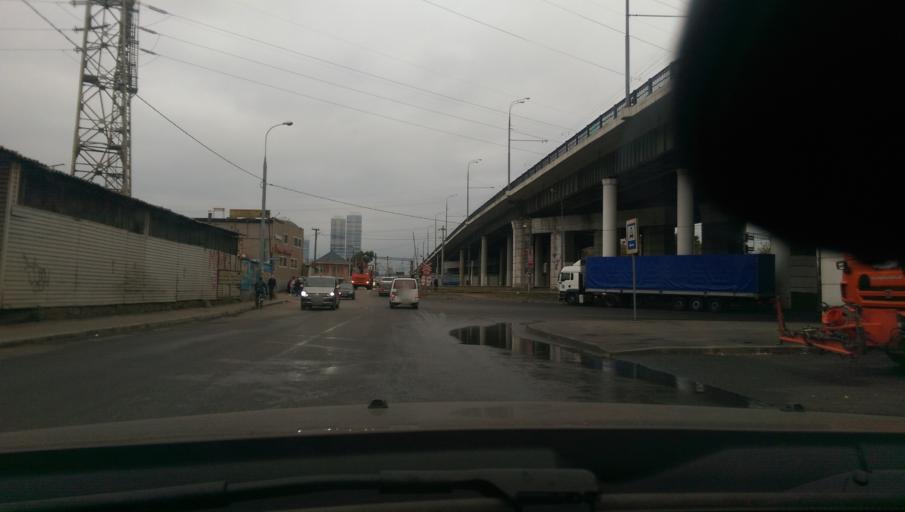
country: RU
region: Moscow
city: Rostokino
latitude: 55.8478
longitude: 37.6734
